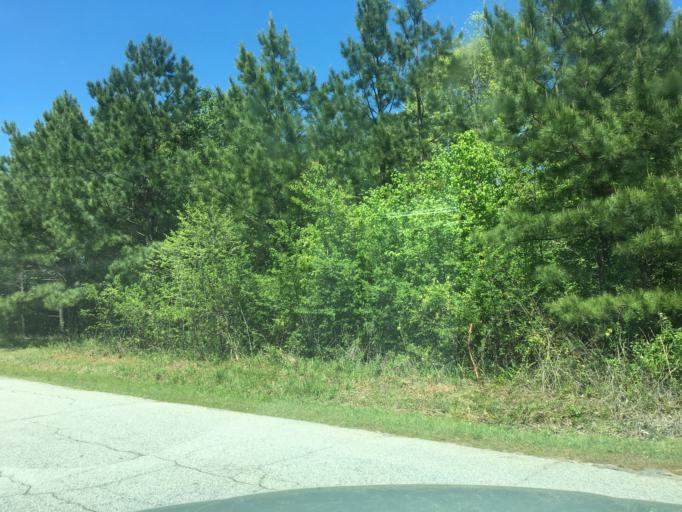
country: US
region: South Carolina
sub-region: Spartanburg County
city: Duncan
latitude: 34.8774
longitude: -82.1765
